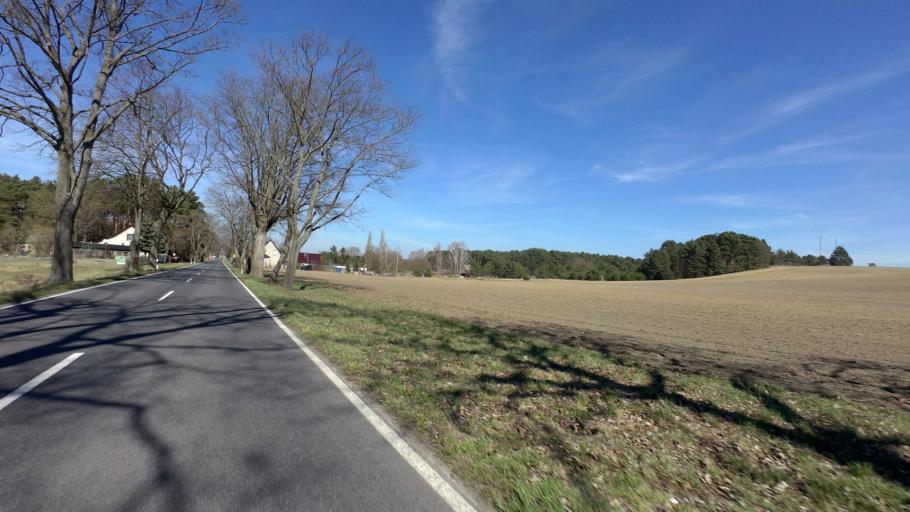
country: DE
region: Brandenburg
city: Storkow
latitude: 52.1894
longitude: 13.9184
